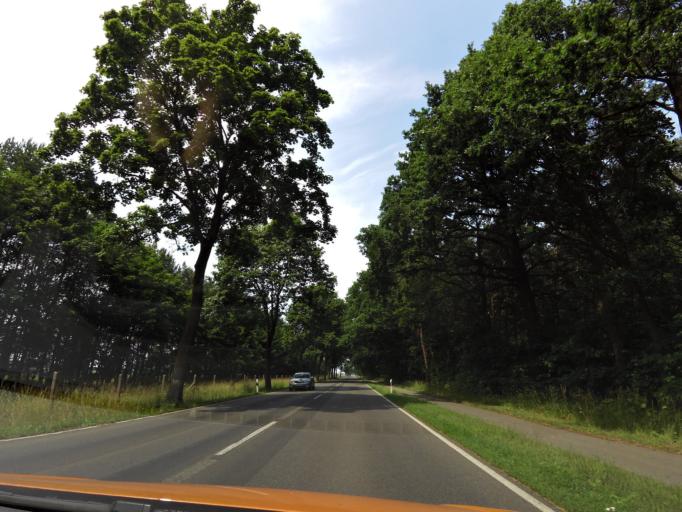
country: DE
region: Brandenburg
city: Kyritz
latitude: 52.9205
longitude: 12.4288
